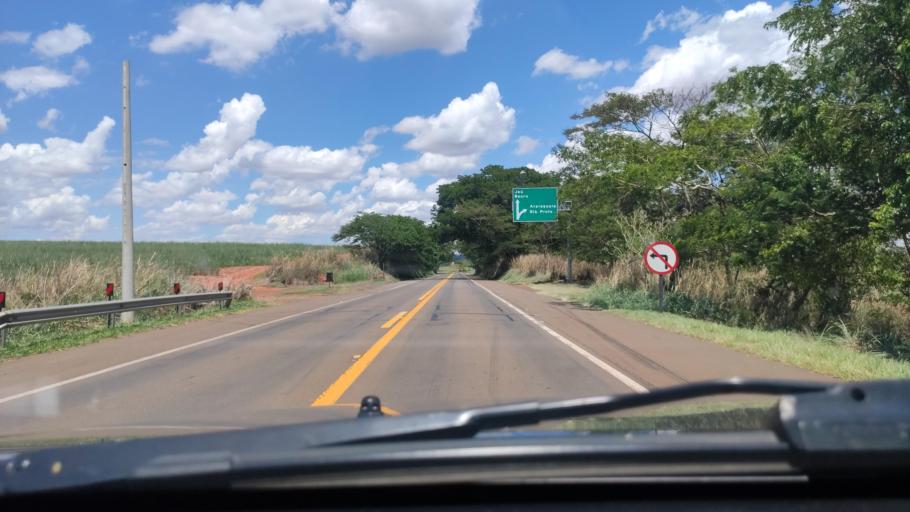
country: BR
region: Sao Paulo
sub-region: Boa Esperanca Do Sul
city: Boa Esperanca do Sul
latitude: -22.0698
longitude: -48.4274
